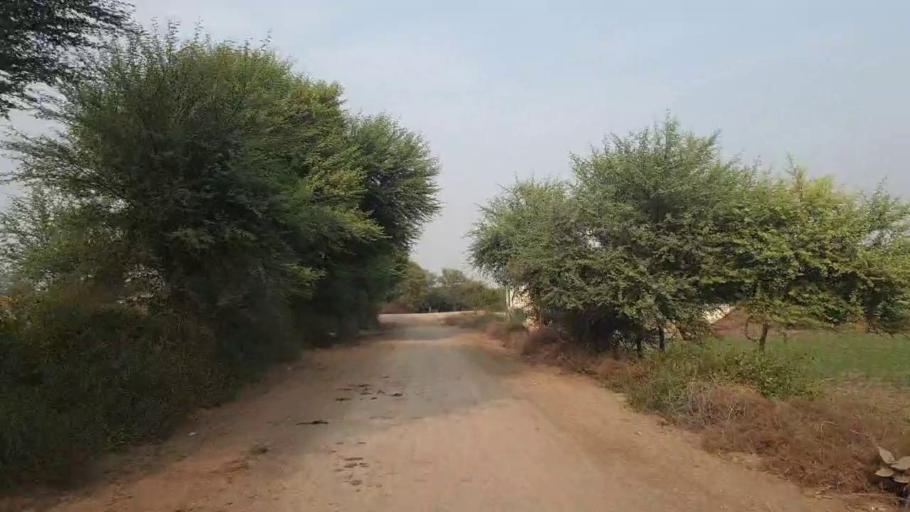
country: PK
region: Sindh
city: Sann
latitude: 26.1264
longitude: 68.0639
